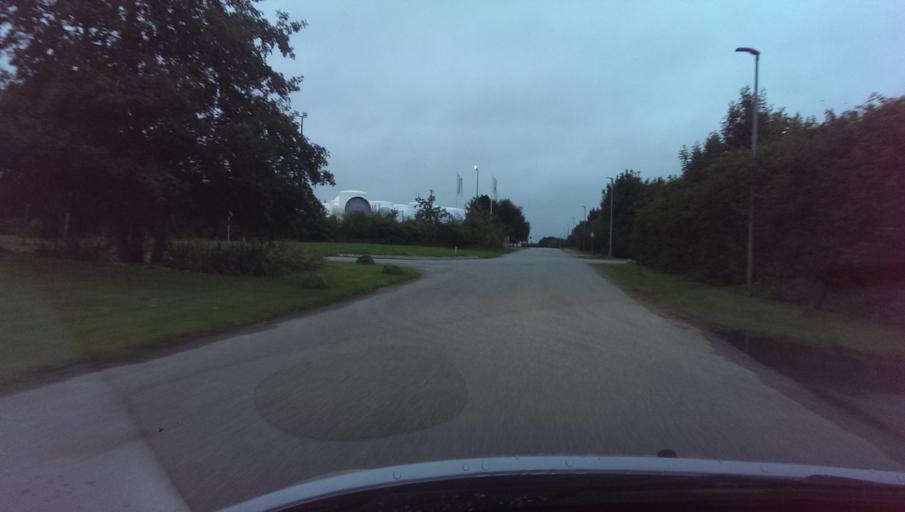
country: DK
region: South Denmark
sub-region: Varde Kommune
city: Olgod
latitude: 55.8157
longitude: 8.6367
